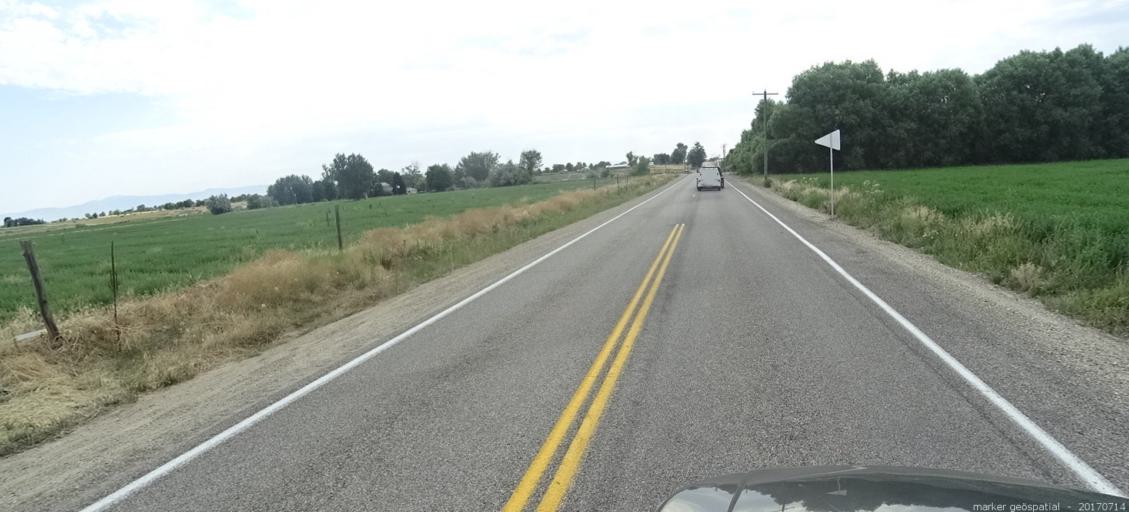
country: US
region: Idaho
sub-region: Ada County
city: Kuna
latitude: 43.4737
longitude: -116.3731
